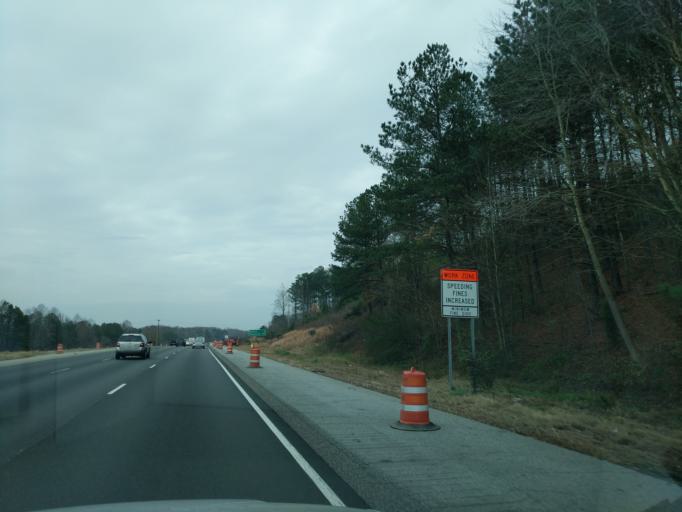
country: US
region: Georgia
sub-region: Gwinnett County
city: Suwanee
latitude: 34.0468
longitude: -84.0259
